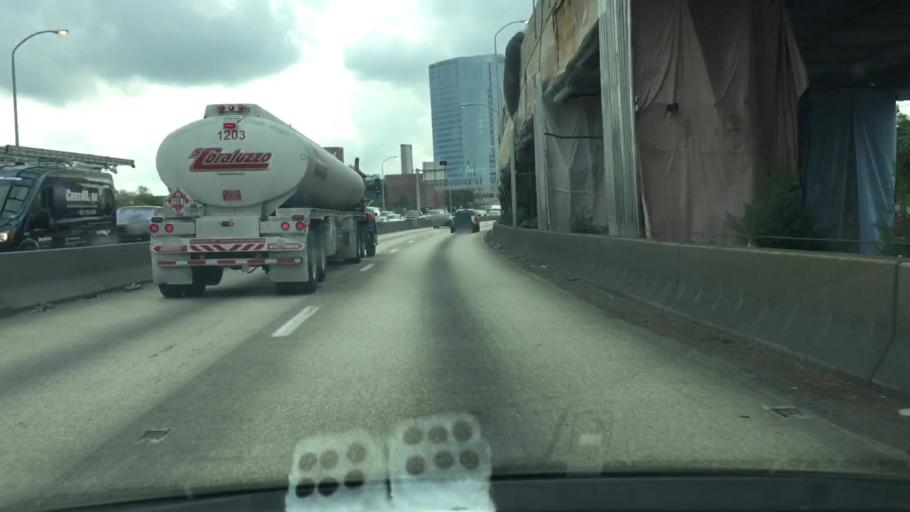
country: US
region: Pennsylvania
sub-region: Philadelphia County
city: Philadelphia
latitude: 39.9502
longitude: -75.1830
